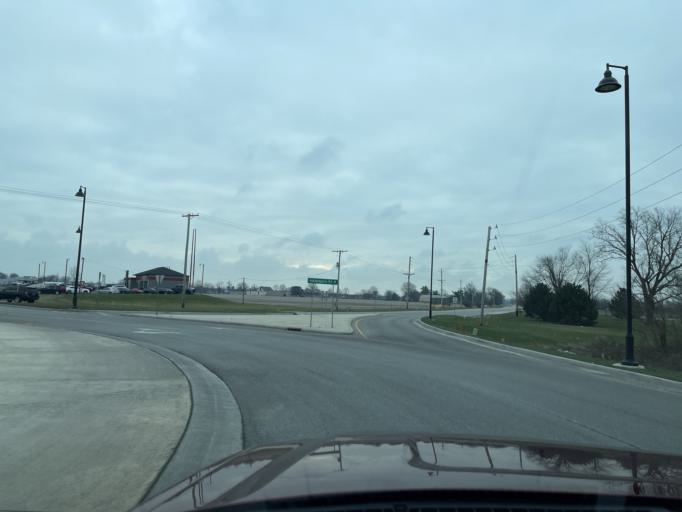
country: US
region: Indiana
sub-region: Boone County
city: Whitestown
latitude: 39.9459
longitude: -86.3588
